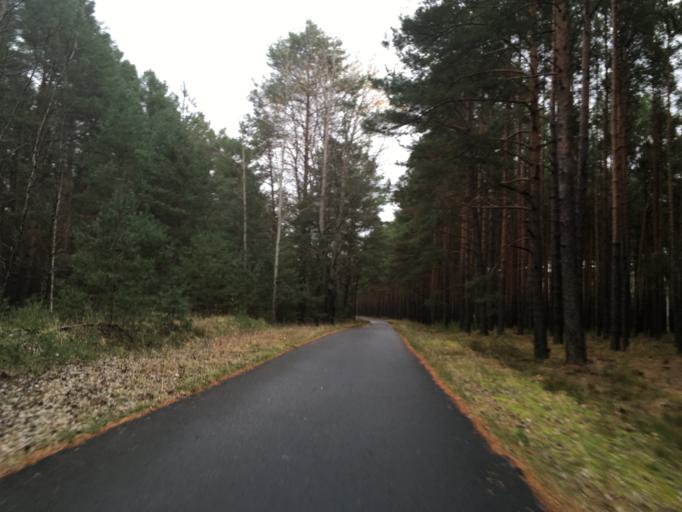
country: DE
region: Brandenburg
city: Mullrose
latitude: 52.2336
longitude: 14.4479
